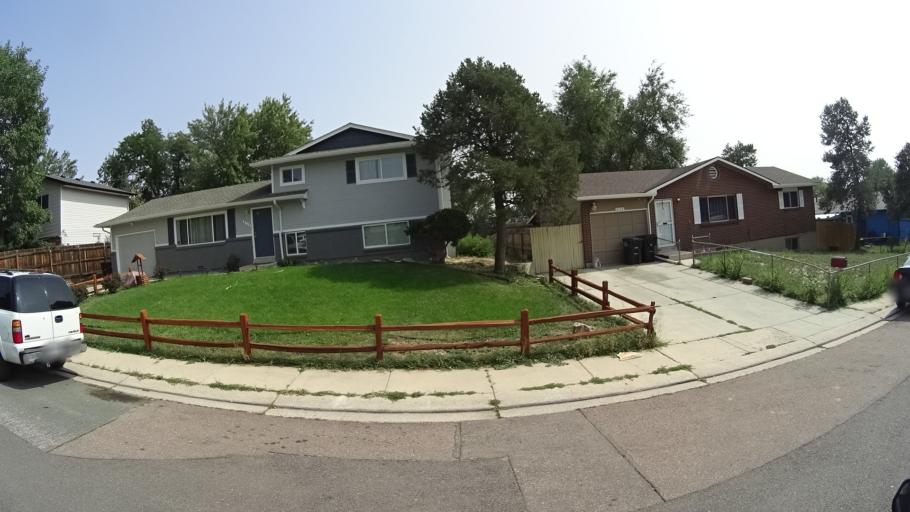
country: US
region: Colorado
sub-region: El Paso County
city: Stratmoor
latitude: 38.8012
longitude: -104.7694
